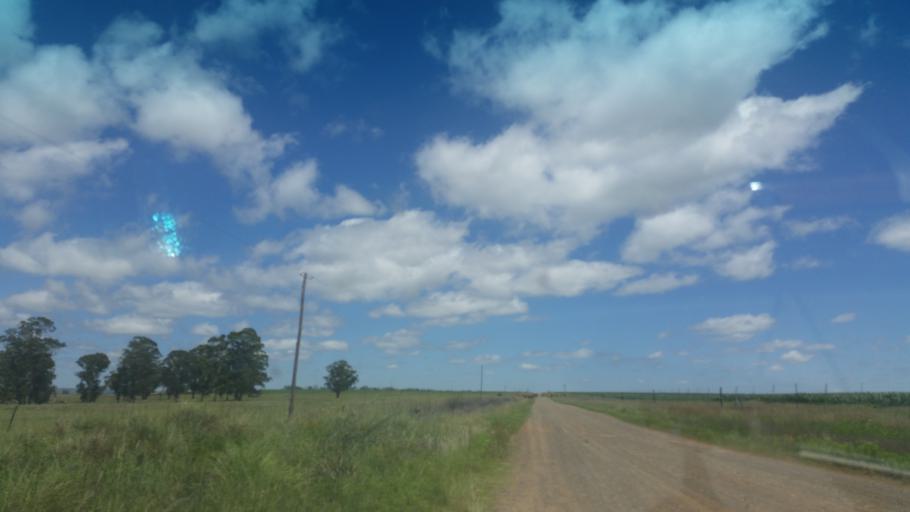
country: ZA
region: Orange Free State
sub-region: Thabo Mofutsanyana District Municipality
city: Harrismith
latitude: -28.1754
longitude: 29.0166
